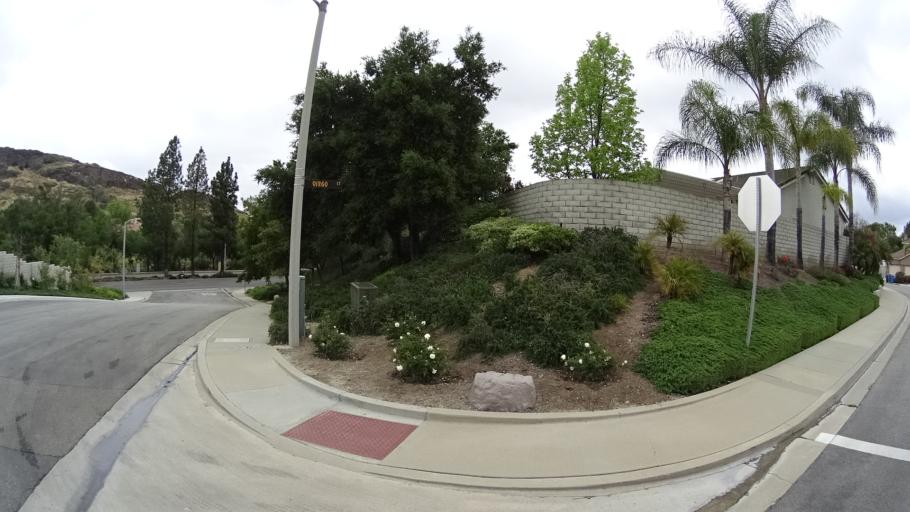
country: US
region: California
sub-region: Ventura County
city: Moorpark
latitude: 34.2236
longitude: -118.8845
